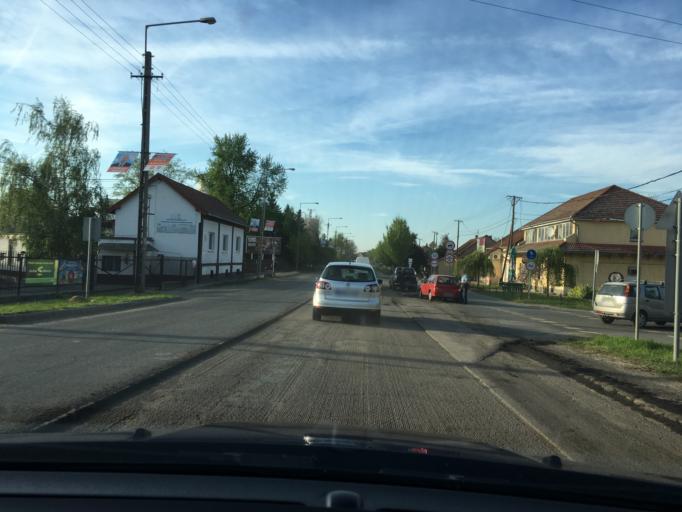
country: HU
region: Hajdu-Bihar
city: Berettyoujfalu
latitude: 47.2114
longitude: 21.5369
